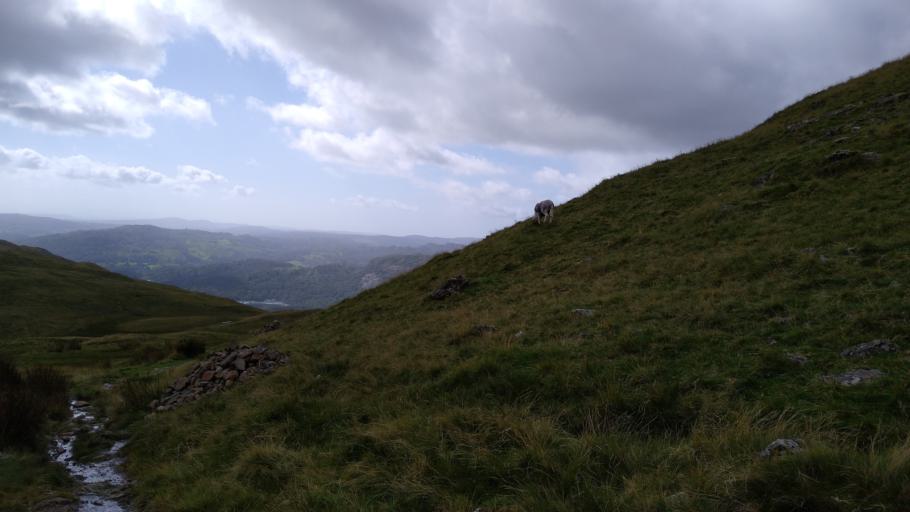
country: GB
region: England
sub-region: Cumbria
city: Ambleside
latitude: 54.4578
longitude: -3.0641
